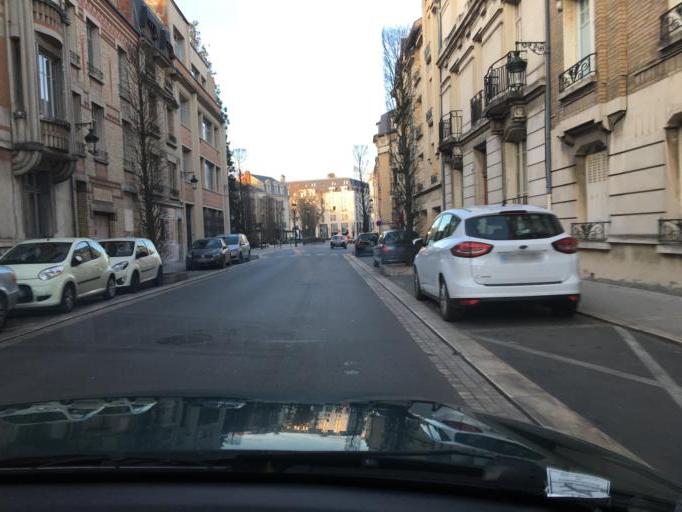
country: FR
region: Centre
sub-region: Departement du Loiret
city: Orleans
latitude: 47.9040
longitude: 1.9098
